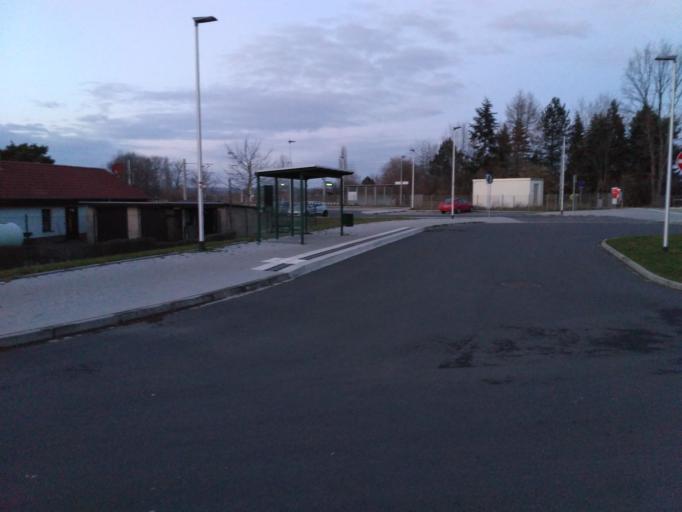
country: DE
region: Saxony
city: Weinbohla
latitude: 51.1474
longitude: 13.5517
